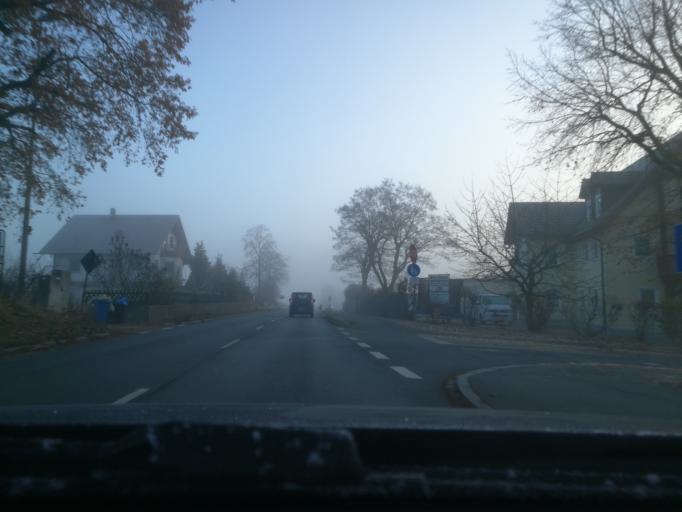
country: DE
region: Bavaria
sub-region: Regierungsbezirk Mittelfranken
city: Obermichelbach
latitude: 49.5635
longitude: 10.9261
